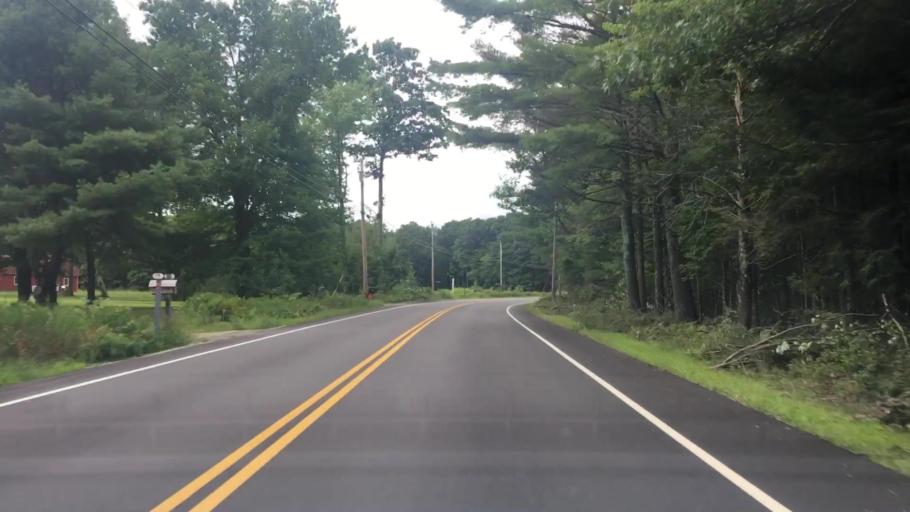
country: US
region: Maine
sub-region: York County
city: West Kennebunk
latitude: 43.4743
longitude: -70.6024
